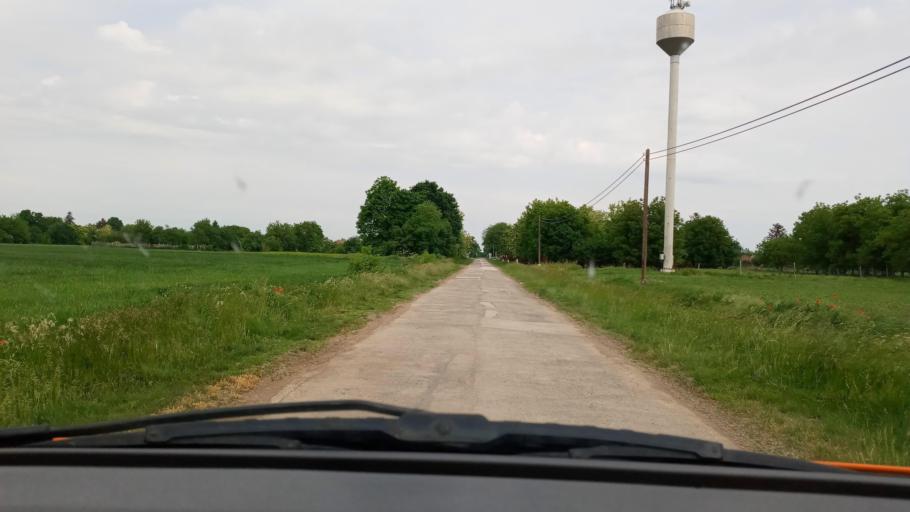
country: HU
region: Baranya
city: Vajszlo
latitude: 45.9259
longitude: 18.0228
